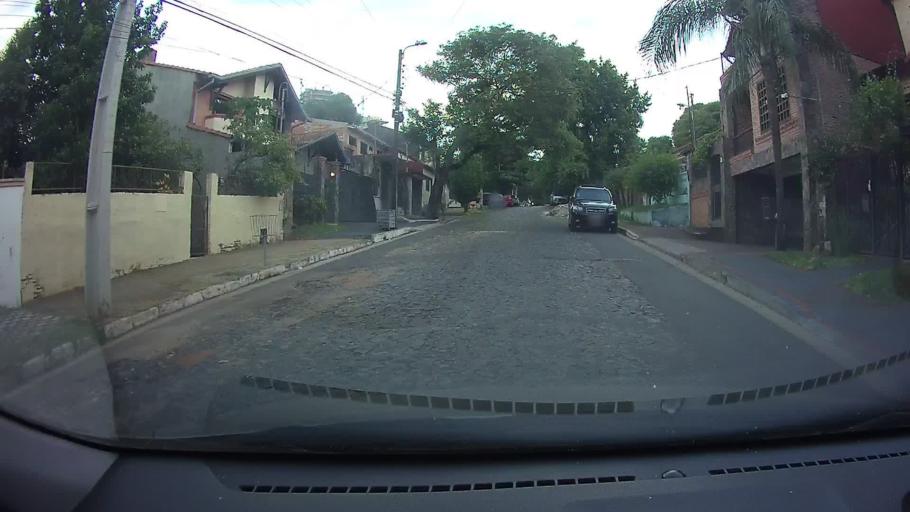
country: PY
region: Asuncion
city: Asuncion
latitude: -25.2686
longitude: -57.5711
